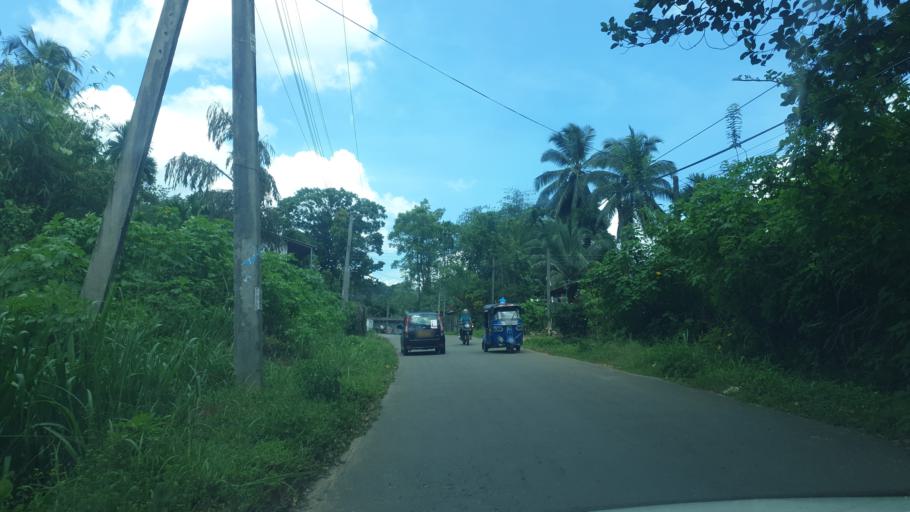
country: LK
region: Sabaragamuwa
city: Ratnapura
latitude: 6.4926
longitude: 80.3973
